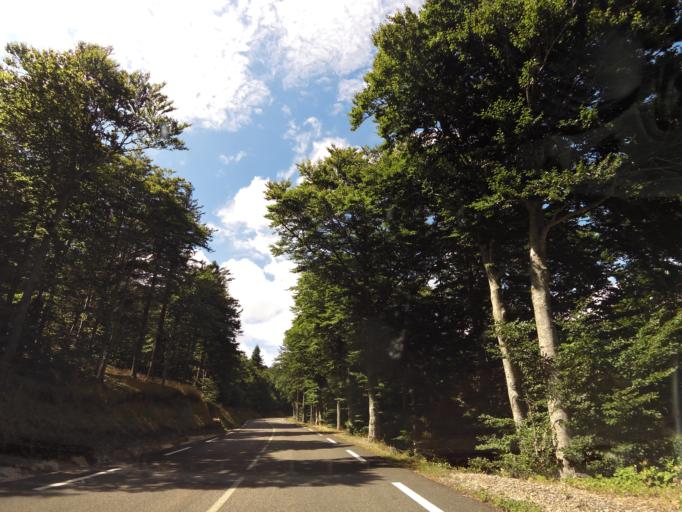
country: FR
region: Languedoc-Roussillon
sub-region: Departement du Gard
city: Valleraugue
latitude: 44.1060
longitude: 3.5481
